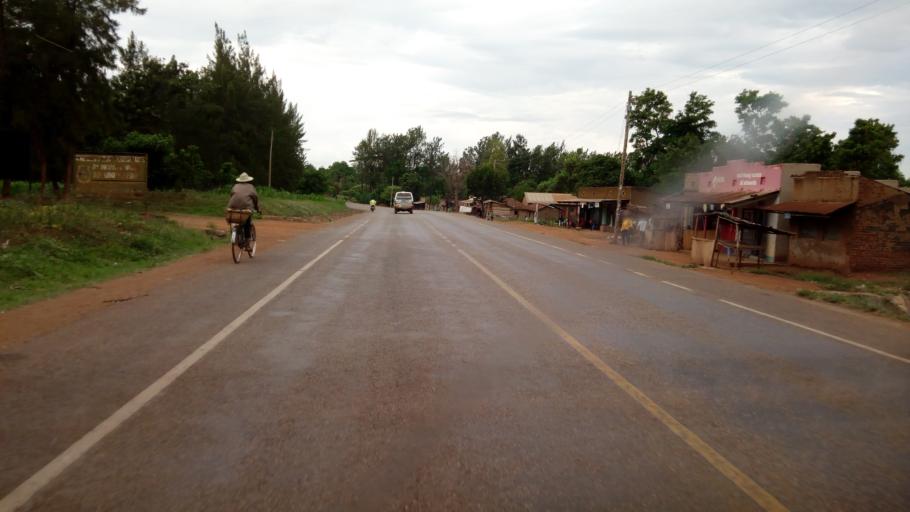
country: UG
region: Eastern Region
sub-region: Mbale District
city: Mbale
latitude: 1.0303
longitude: 34.1767
